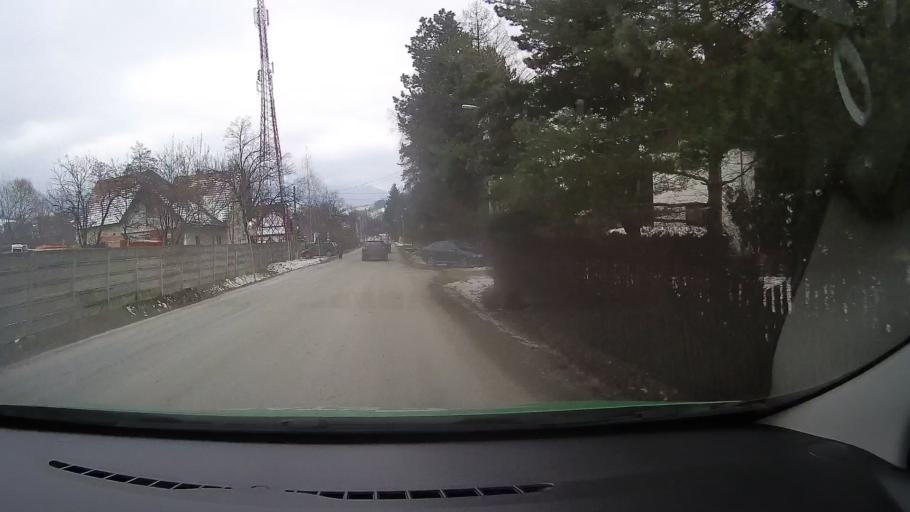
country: RO
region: Brasov
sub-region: Comuna Bran
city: Bran
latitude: 45.5240
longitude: 25.3654
